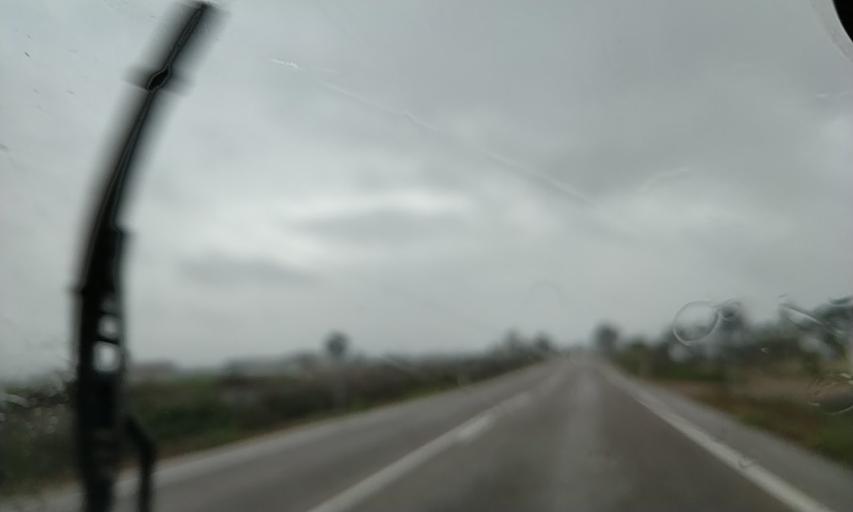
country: ES
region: Extremadura
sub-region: Provincia de Badajoz
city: Badajoz
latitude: 38.9279
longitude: -6.9335
